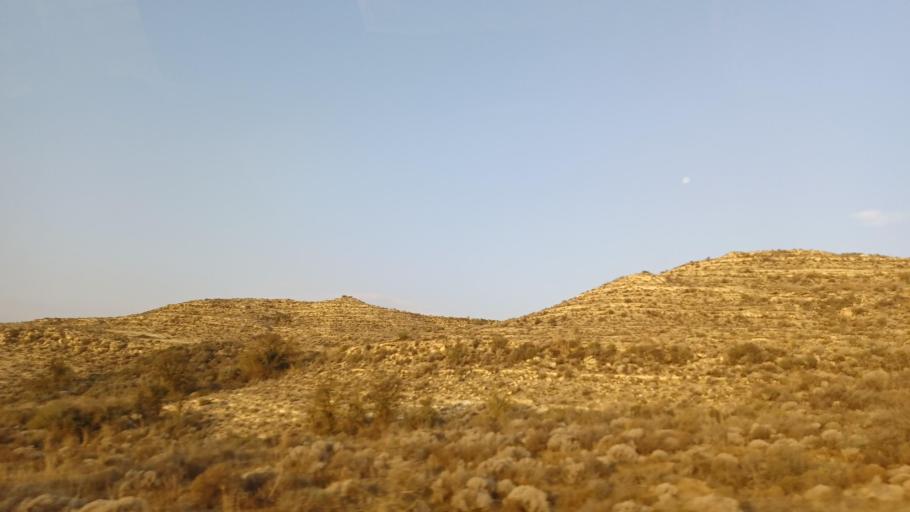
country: CY
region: Larnaka
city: Athienou
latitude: 35.0115
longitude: 33.5284
